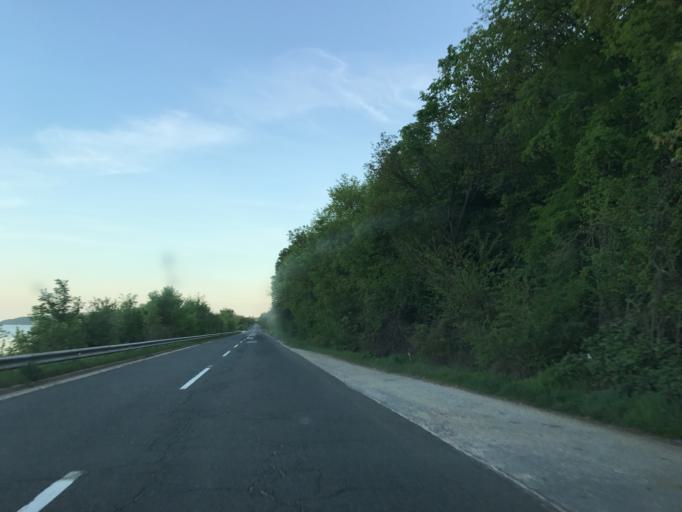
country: RO
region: Mehedinti
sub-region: Comuna Gogosu
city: Ostrovu Mare
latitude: 44.4611
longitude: 22.4513
